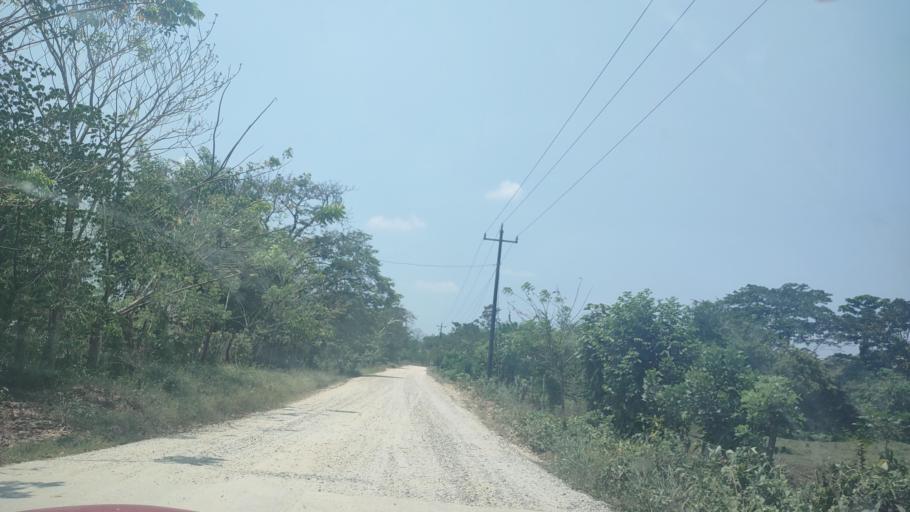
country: MX
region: Tabasco
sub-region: Huimanguillo
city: Francisco Rueda
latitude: 17.6904
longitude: -94.0486
